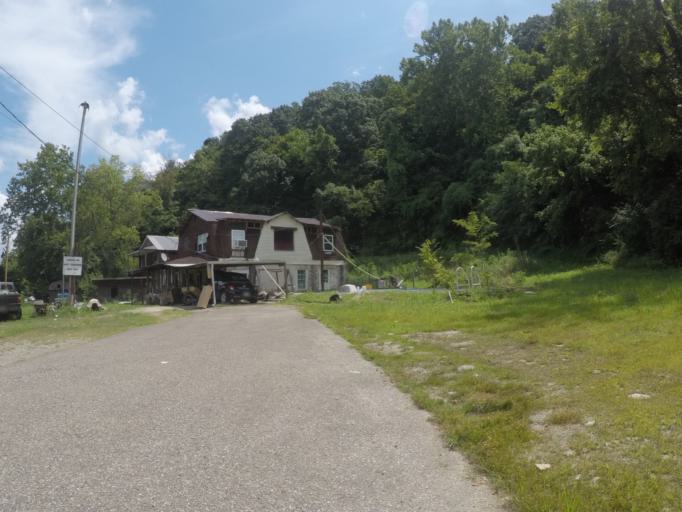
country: US
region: West Virginia
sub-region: Cabell County
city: Pea Ridge
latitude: 38.4277
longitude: -82.3730
